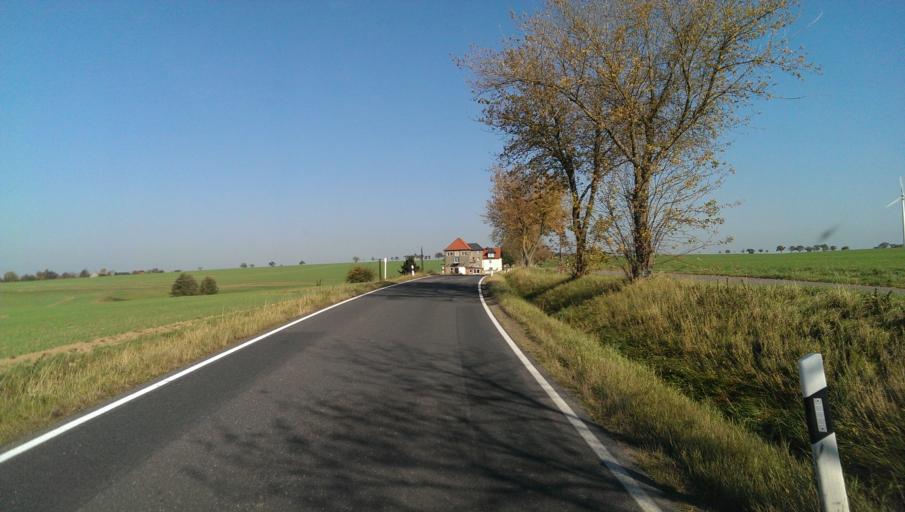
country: DE
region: Saxony
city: Waldheim
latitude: 51.0859
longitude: 13.0391
